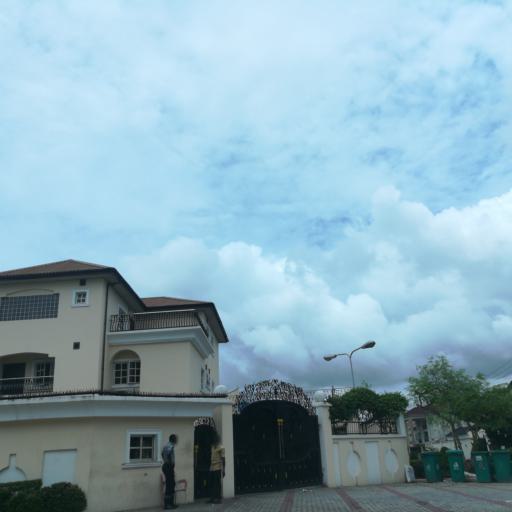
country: NG
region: Lagos
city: Ikoyi
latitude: 6.4438
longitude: 3.4624
